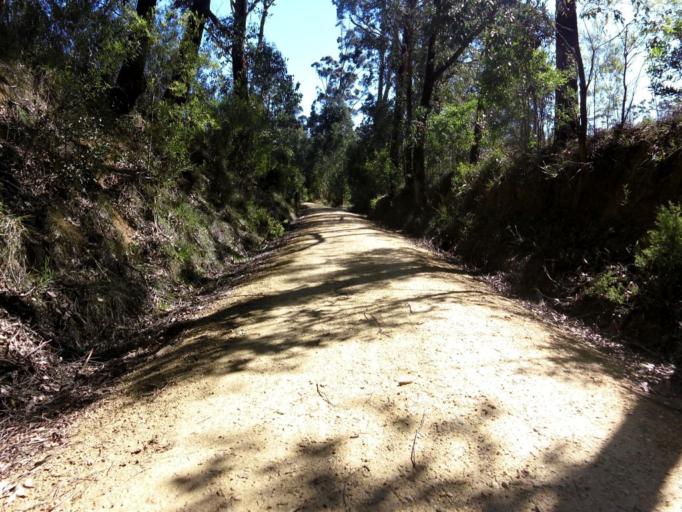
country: AU
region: Victoria
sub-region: Latrobe
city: Moe
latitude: -38.3744
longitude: 146.2319
